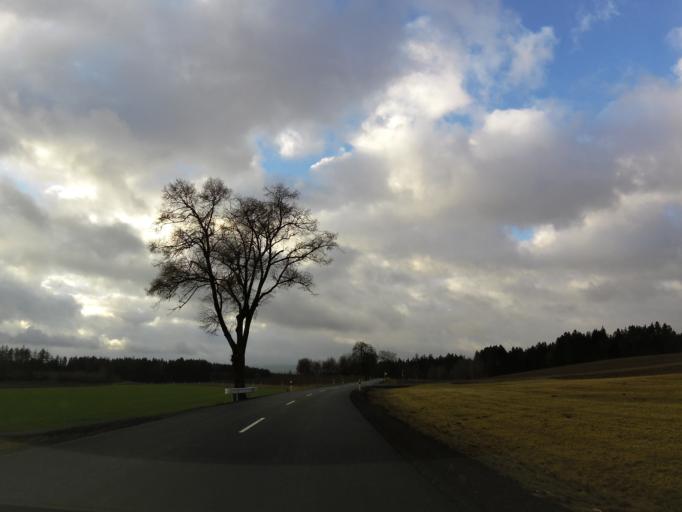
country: DE
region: Bavaria
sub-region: Upper Franconia
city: Hochstadt bei Thiersheim
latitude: 50.0725
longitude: 12.0473
